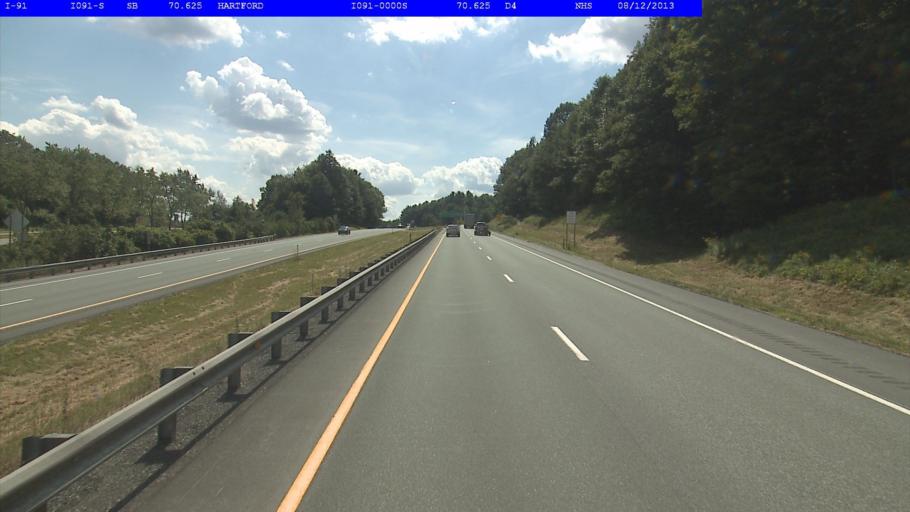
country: US
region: Vermont
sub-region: Windsor County
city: White River Junction
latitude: 43.6507
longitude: -72.3337
